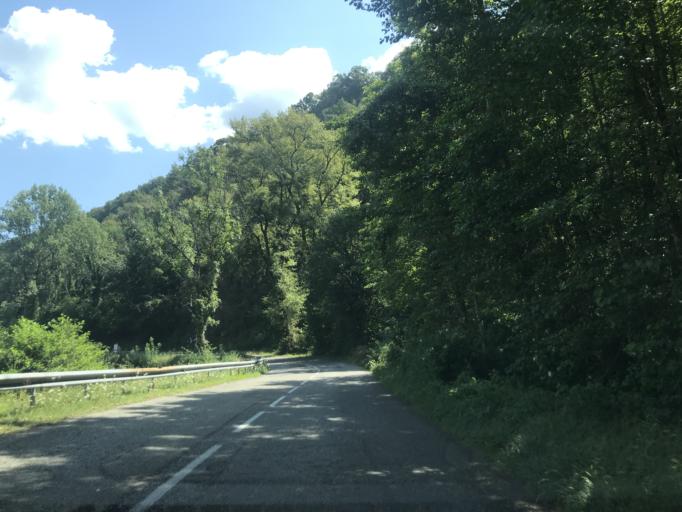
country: FR
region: Rhone-Alpes
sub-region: Departement de la Savoie
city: Chatillon
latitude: 45.8140
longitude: 5.8042
